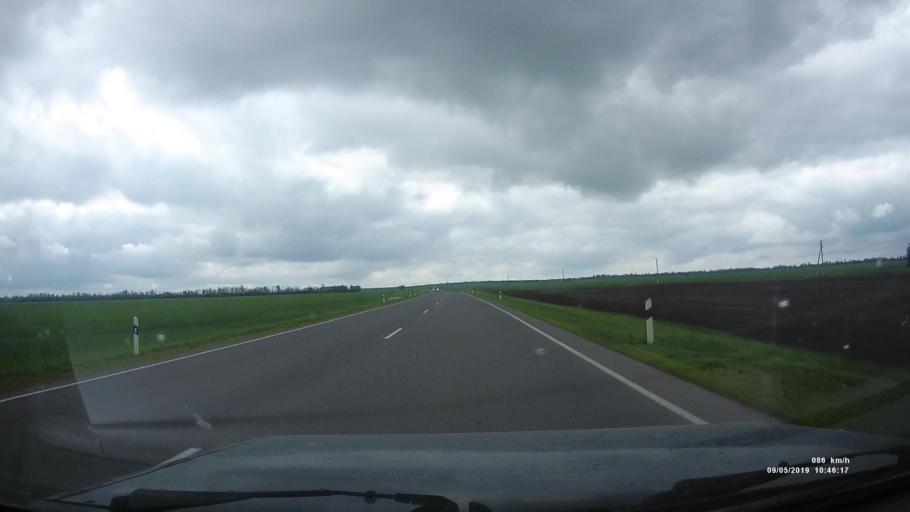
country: RU
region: Rostov
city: Peshkovo
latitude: 46.9868
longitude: 39.3579
